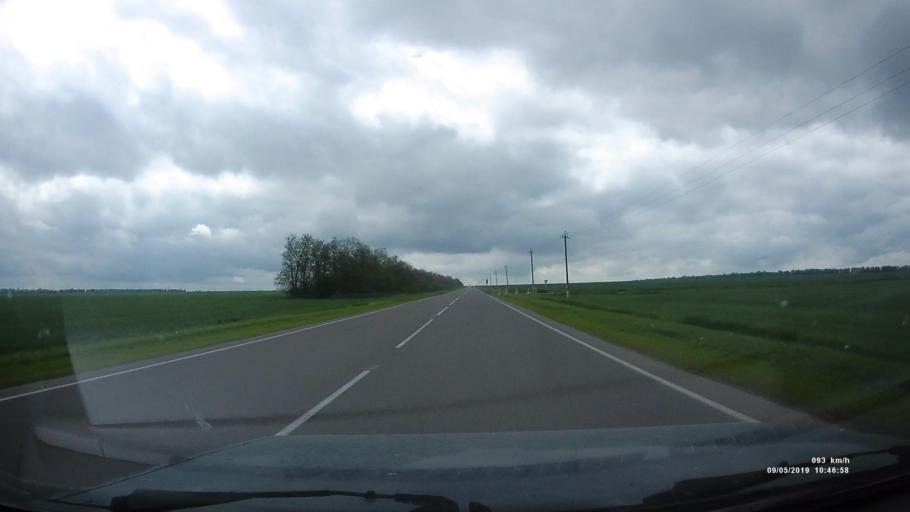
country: RU
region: Rostov
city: Peshkovo
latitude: 46.9774
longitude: 39.3557
